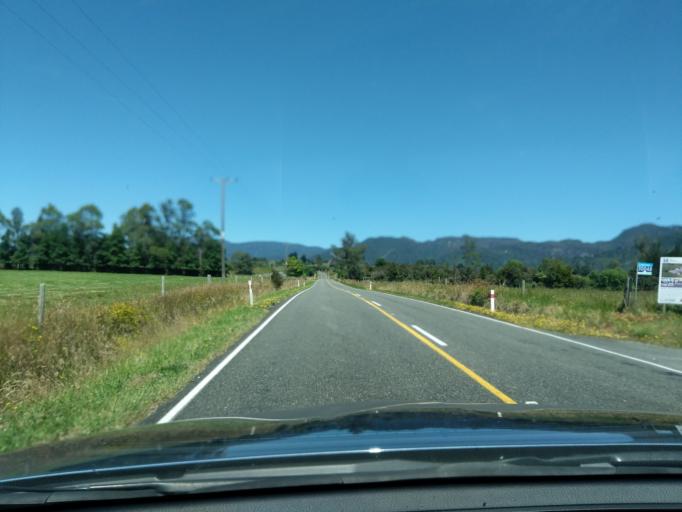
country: NZ
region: Tasman
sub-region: Tasman District
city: Takaka
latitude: -40.6855
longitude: 172.6556
